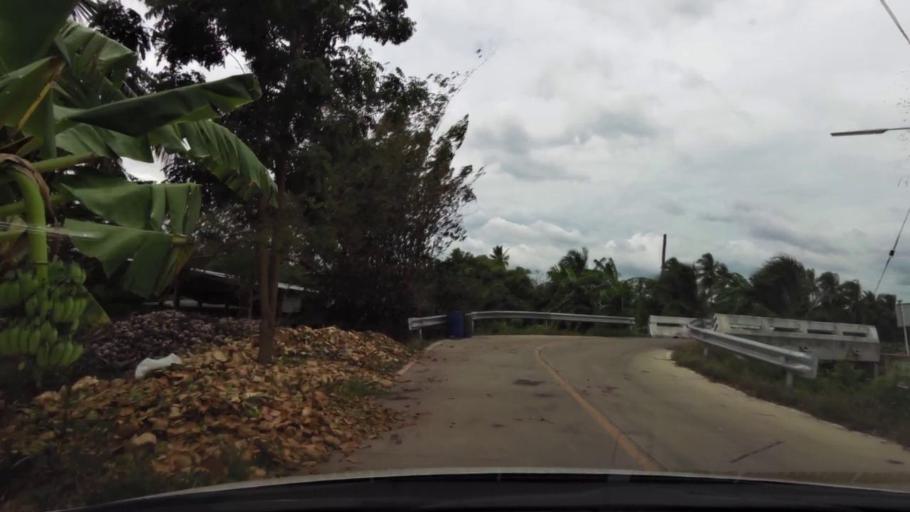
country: TH
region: Ratchaburi
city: Damnoen Saduak
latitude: 13.5604
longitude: 100.0197
